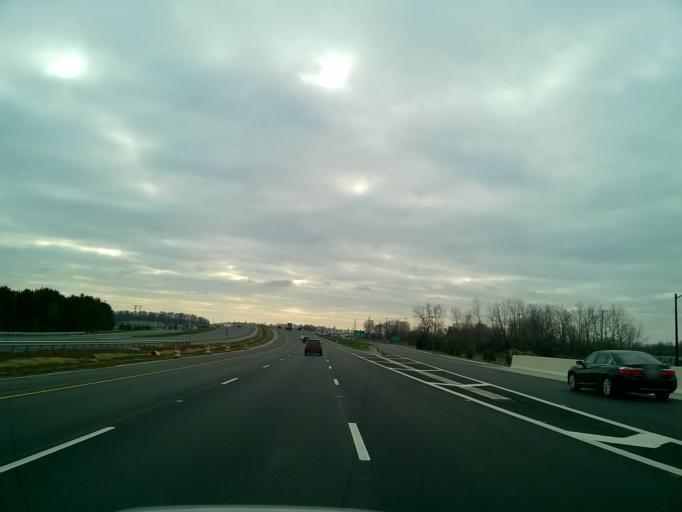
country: US
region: Indiana
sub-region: Hamilton County
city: Westfield
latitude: 40.0462
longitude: -86.1359
